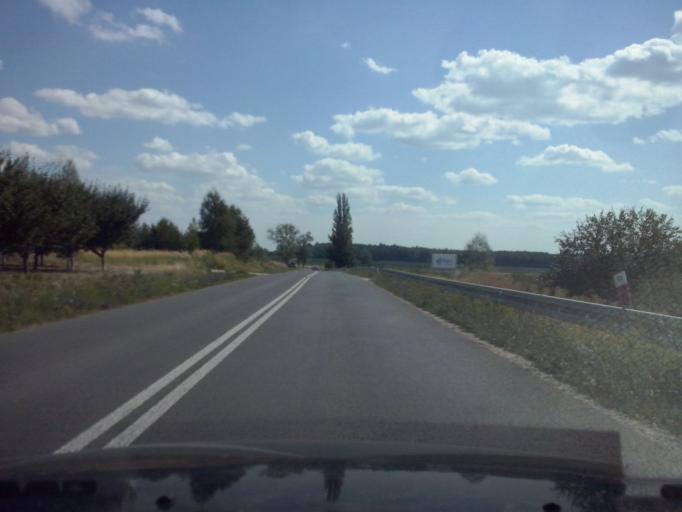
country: PL
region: Swietokrzyskie
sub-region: Powiat staszowski
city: Szydlow
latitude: 50.5853
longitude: 21.0436
